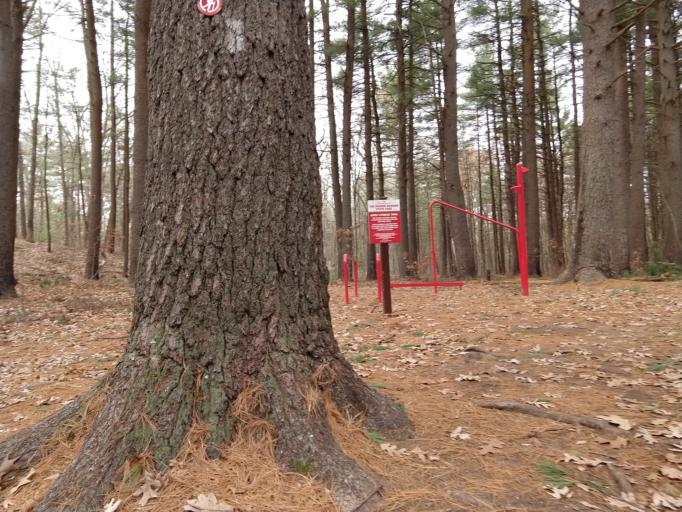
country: US
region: Massachusetts
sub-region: Middlesex County
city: Billerica
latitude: 42.5866
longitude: -71.3021
